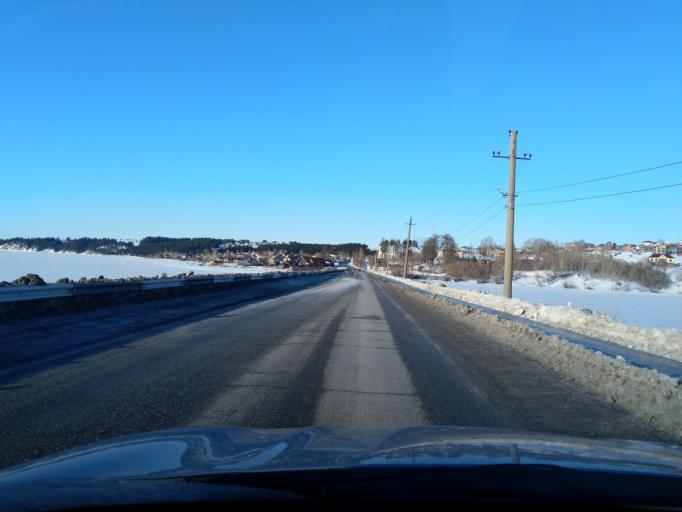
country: RU
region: Perm
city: Polazna
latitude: 58.3025
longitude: 56.4178
